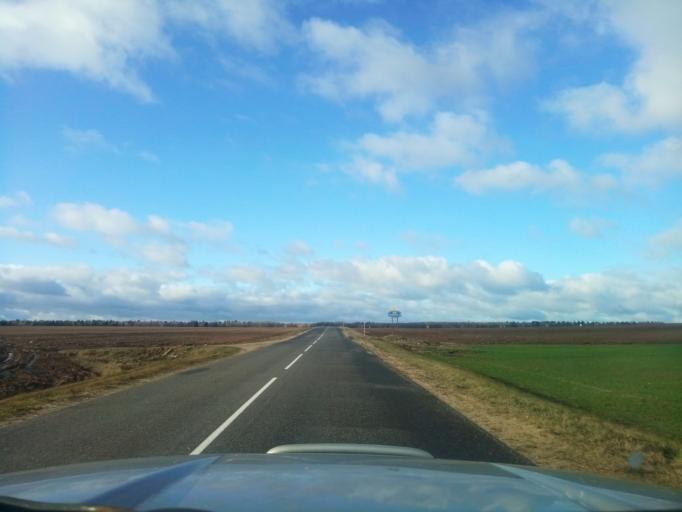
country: BY
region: Minsk
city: Kapyl'
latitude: 53.1695
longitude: 27.0476
